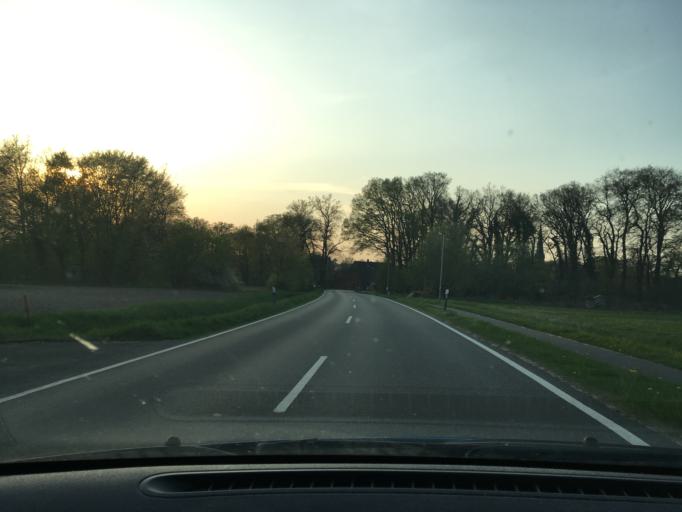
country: DE
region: Lower Saxony
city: Kirchgellersen
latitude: 53.2270
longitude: 10.2960
